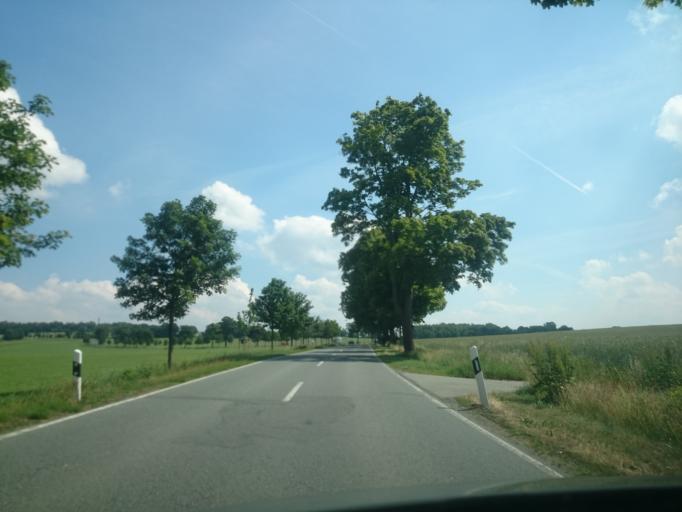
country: DE
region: Saxony
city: Grossolbersdorf
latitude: 50.6884
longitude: 13.1009
